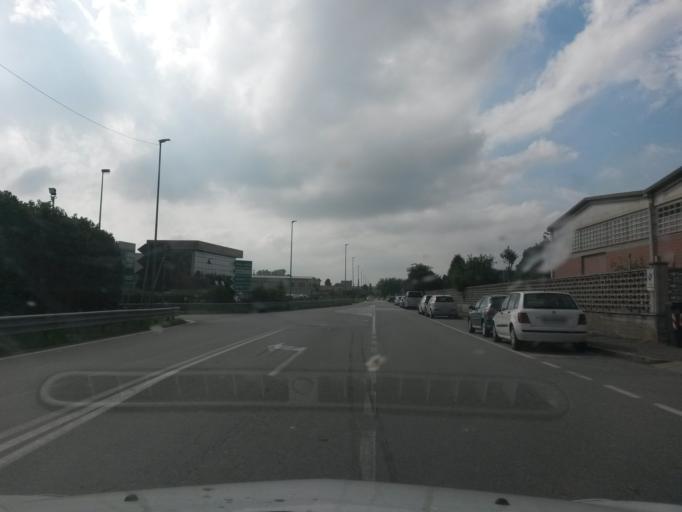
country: IT
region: Piedmont
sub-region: Provincia di Torino
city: Tetti Neirotti
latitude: 45.0634
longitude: 7.5406
